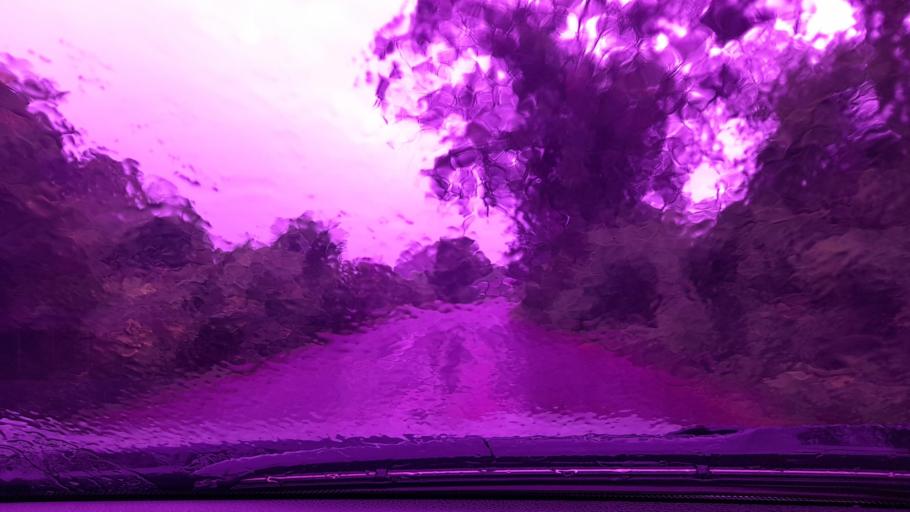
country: ET
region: Oromiya
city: Metu
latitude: 8.3768
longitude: 35.6005
